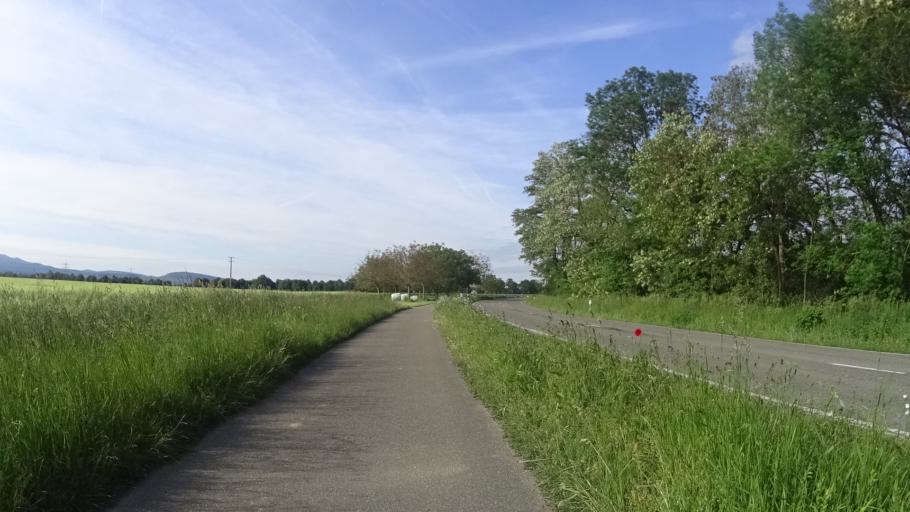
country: DE
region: Baden-Wuerttemberg
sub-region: Freiburg Region
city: Neuenburg am Rhein
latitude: 47.8494
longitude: 7.5833
